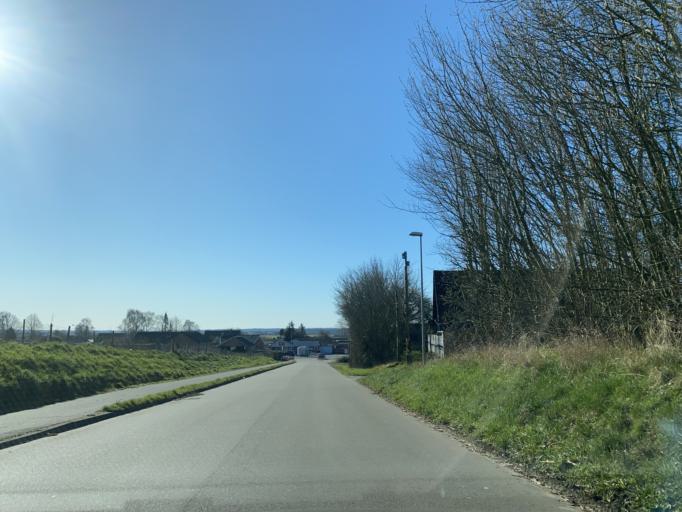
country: DK
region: Central Jutland
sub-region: Skanderborg Kommune
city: Skovby
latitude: 56.1856
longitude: 9.9626
